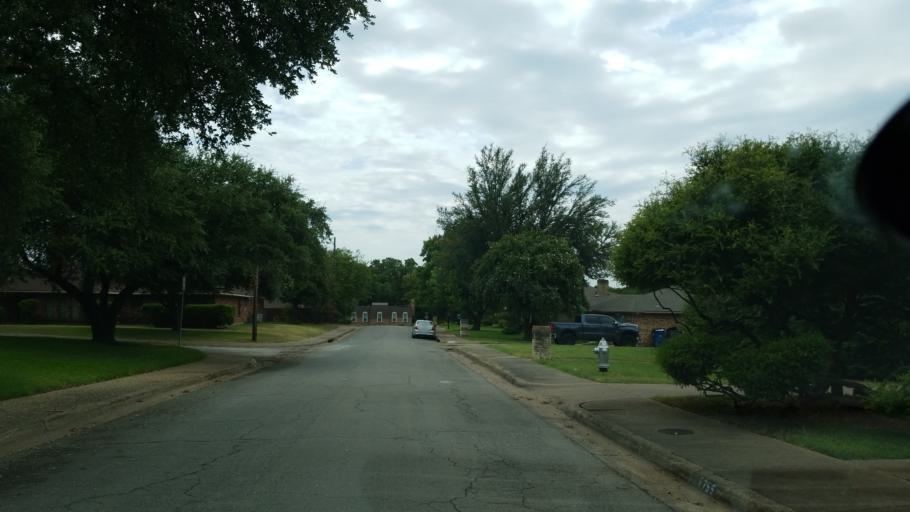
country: US
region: Texas
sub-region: Dallas County
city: Duncanville
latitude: 32.6656
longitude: -96.8565
